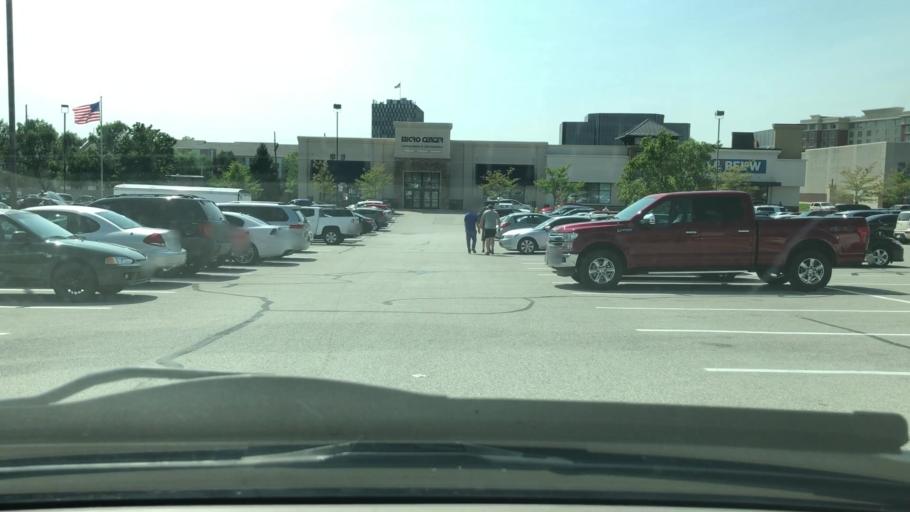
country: US
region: Missouri
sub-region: Saint Louis County
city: Brentwood
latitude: 38.6262
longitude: -90.3416
